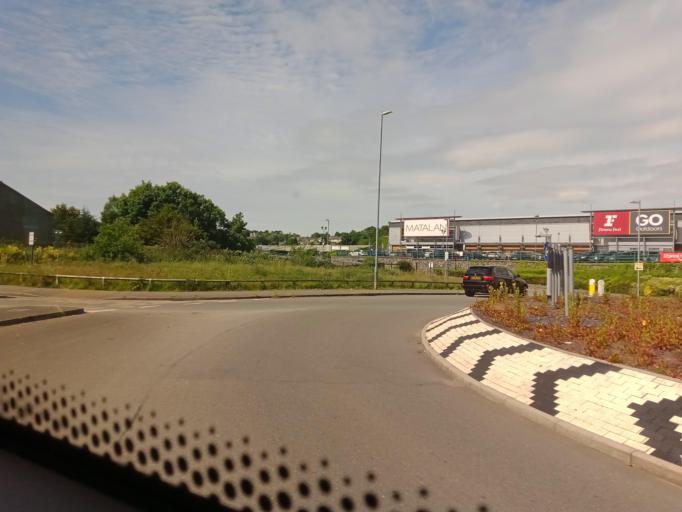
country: GB
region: Wales
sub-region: Gwynedd
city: Bangor
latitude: 53.2174
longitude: -4.1407
